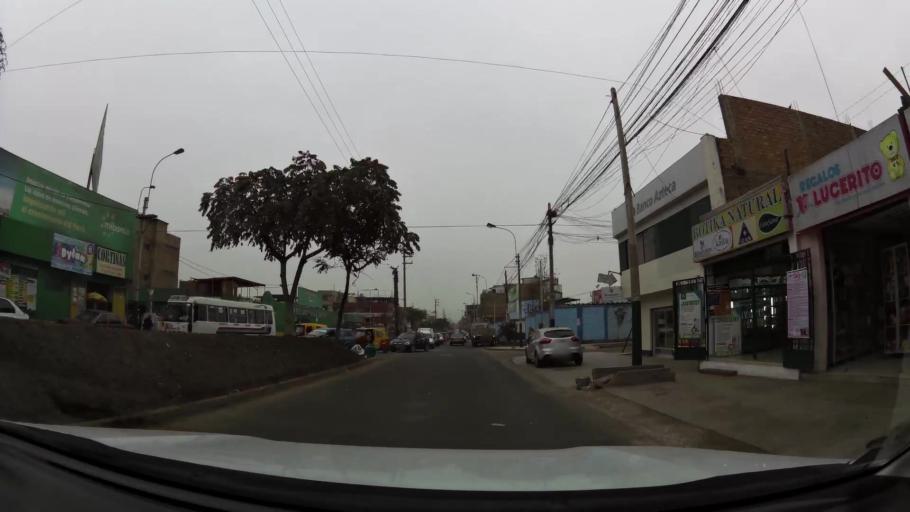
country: PE
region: Lima
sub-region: Lima
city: Surco
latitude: -12.1706
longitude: -76.9682
